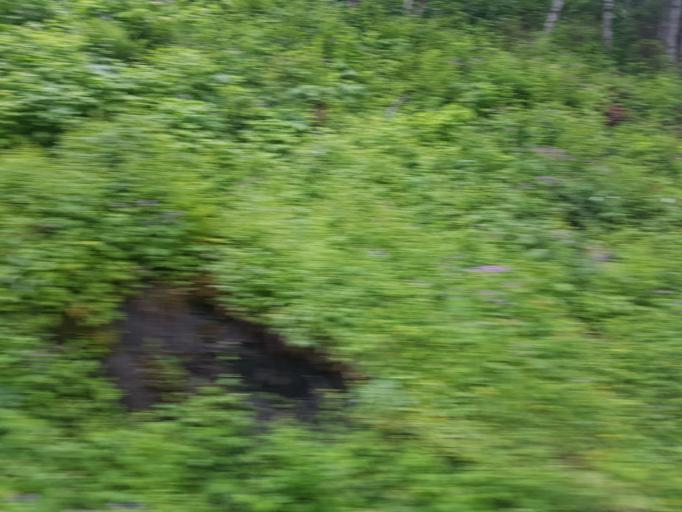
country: NO
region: Sor-Trondelag
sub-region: Selbu
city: Mebonden
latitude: 63.3224
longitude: 11.0852
